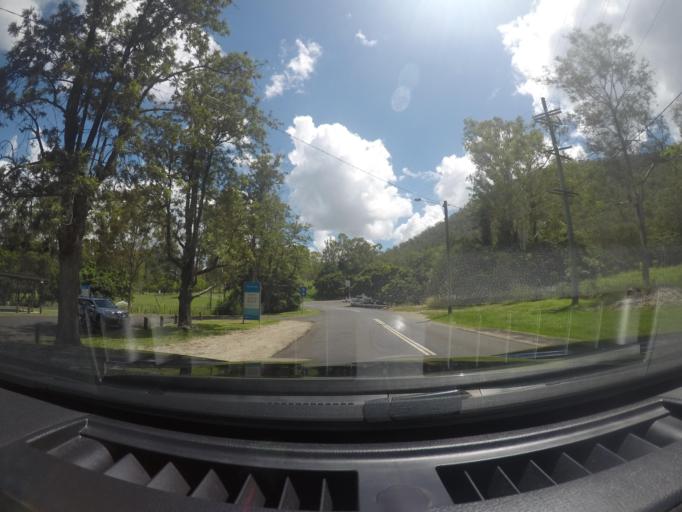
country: AU
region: Queensland
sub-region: Moreton Bay
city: Woodford
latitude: -27.1194
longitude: 152.5508
